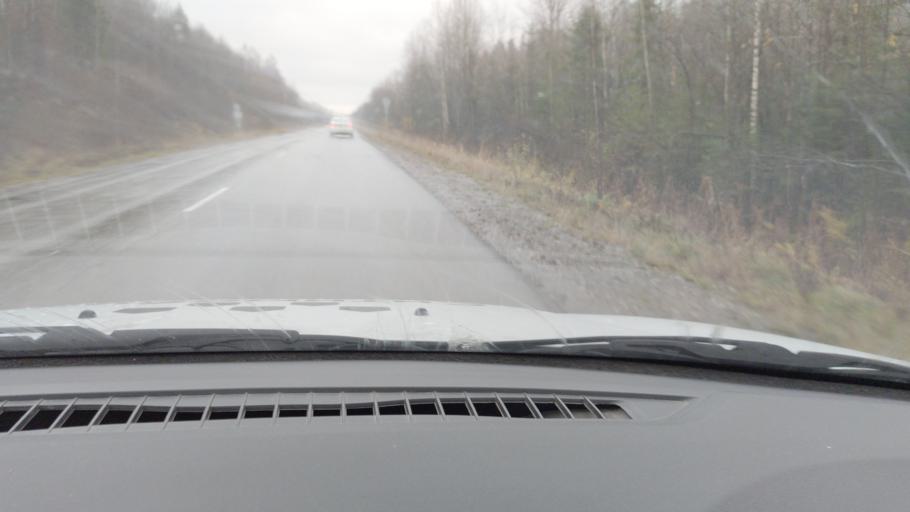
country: RU
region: Perm
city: Novyye Lyady
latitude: 58.0302
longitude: 56.6197
